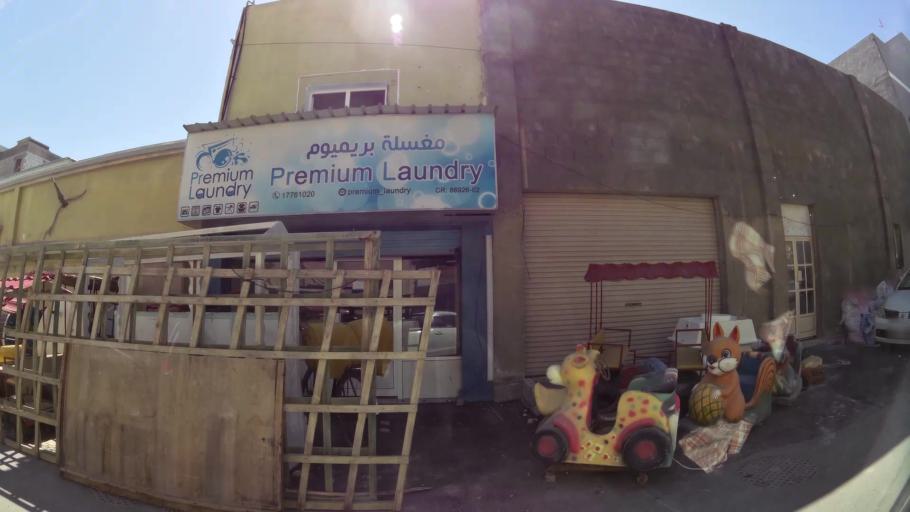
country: BH
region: Muharraq
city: Al Muharraq
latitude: 26.2818
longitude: 50.6377
